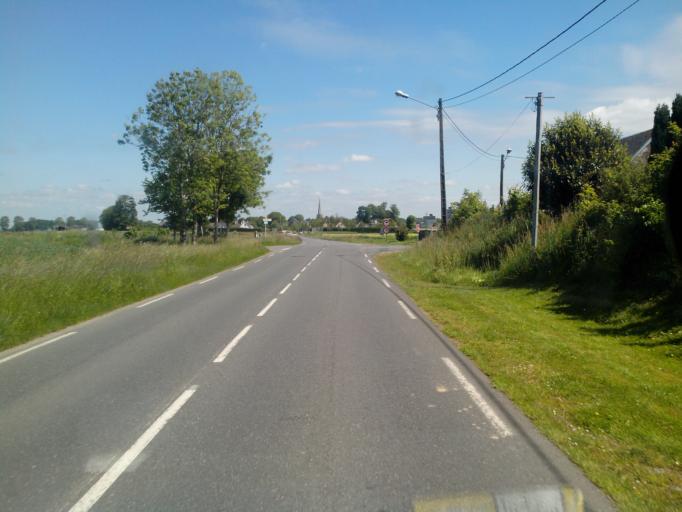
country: FR
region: Haute-Normandie
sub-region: Departement de la Seine-Maritime
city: La Cerlangue
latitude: 49.5108
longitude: 0.4010
